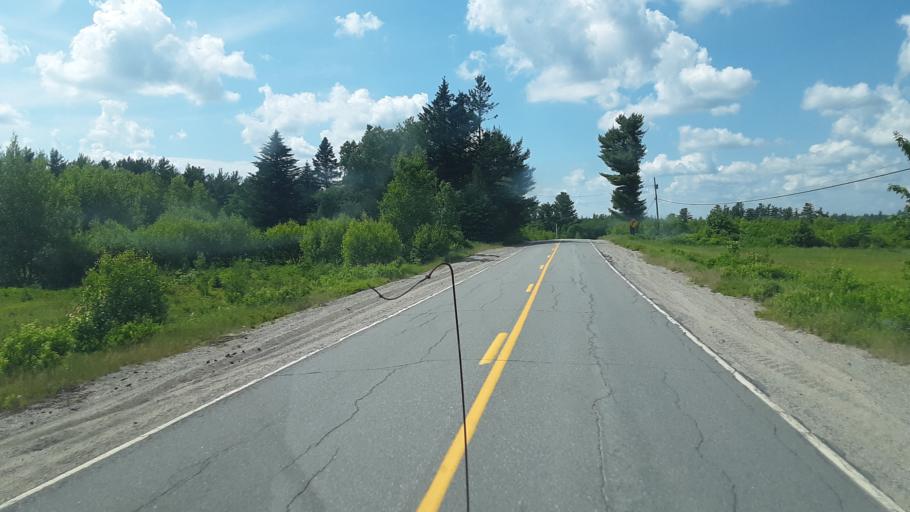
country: US
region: Maine
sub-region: Washington County
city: Machias
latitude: 44.9244
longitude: -67.6589
